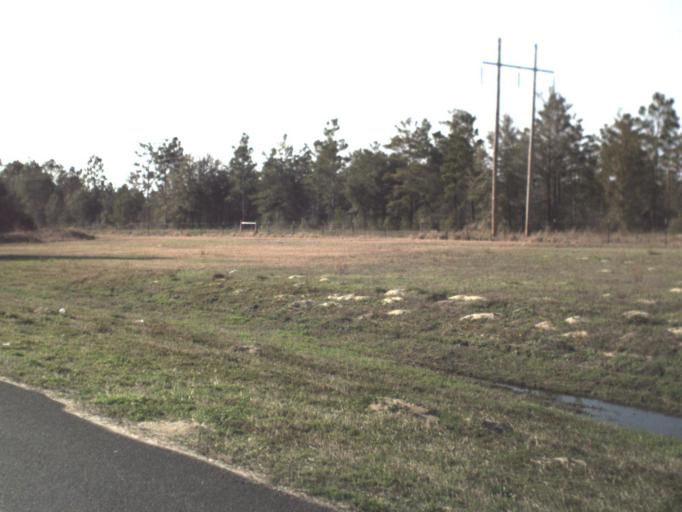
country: US
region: Florida
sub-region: Bay County
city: Lynn Haven
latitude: 30.4390
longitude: -85.7158
